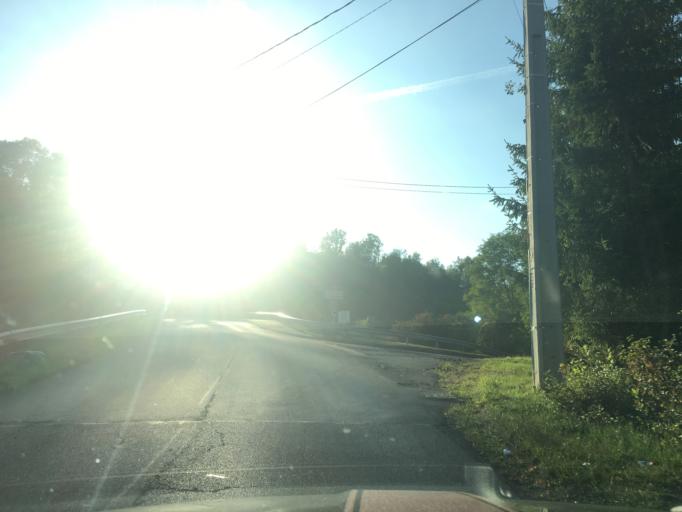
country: FR
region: Lorraine
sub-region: Departement de Meurthe-et-Moselle
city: Hussigny-Godbrange
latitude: 49.4985
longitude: 5.8679
